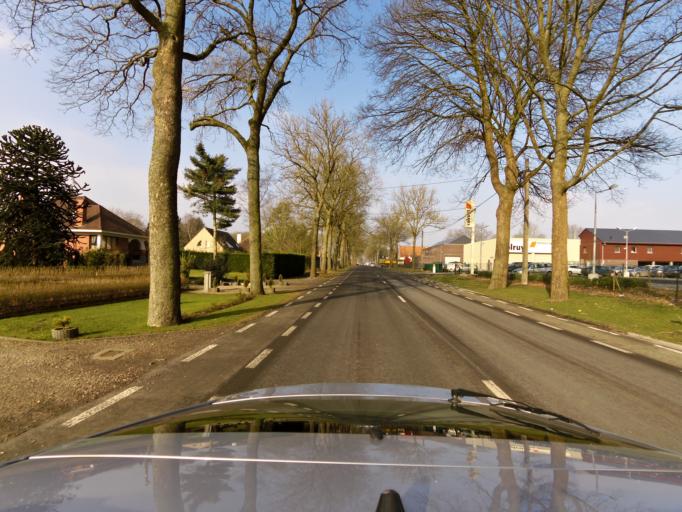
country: BE
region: Wallonia
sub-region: Province du Hainaut
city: Bernissart
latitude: 50.5110
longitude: 3.6817
